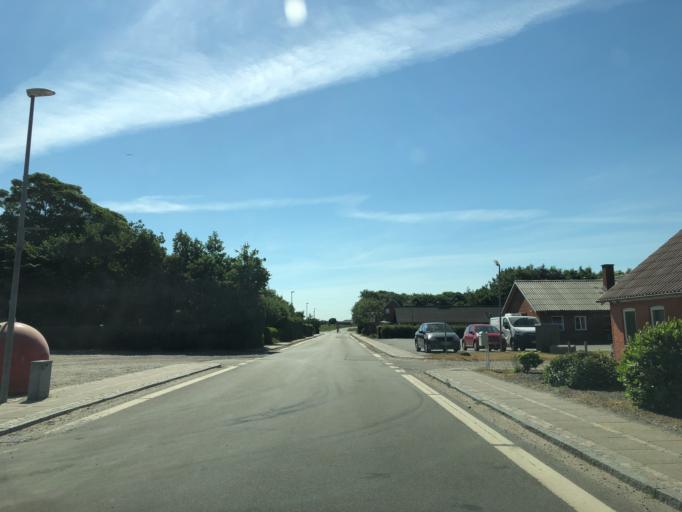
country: DK
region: Central Jutland
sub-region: Struer Kommune
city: Struer
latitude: 56.4326
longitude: 8.5139
